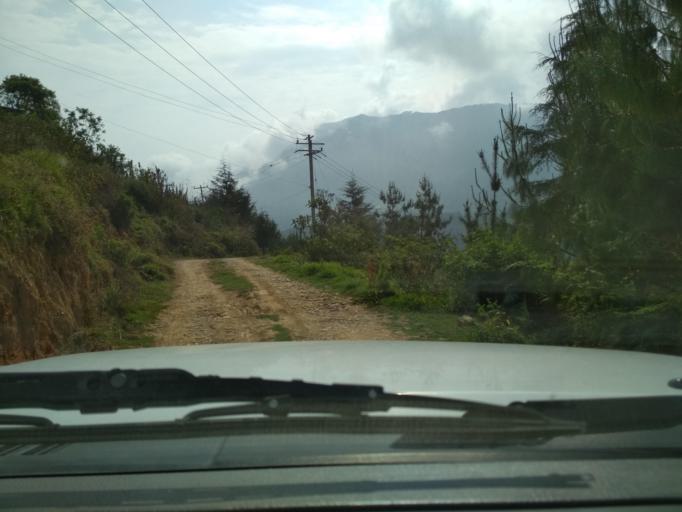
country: MX
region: Veracruz
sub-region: Soledad Atzompa
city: Tlatilpa
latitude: 18.7520
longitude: -97.1530
